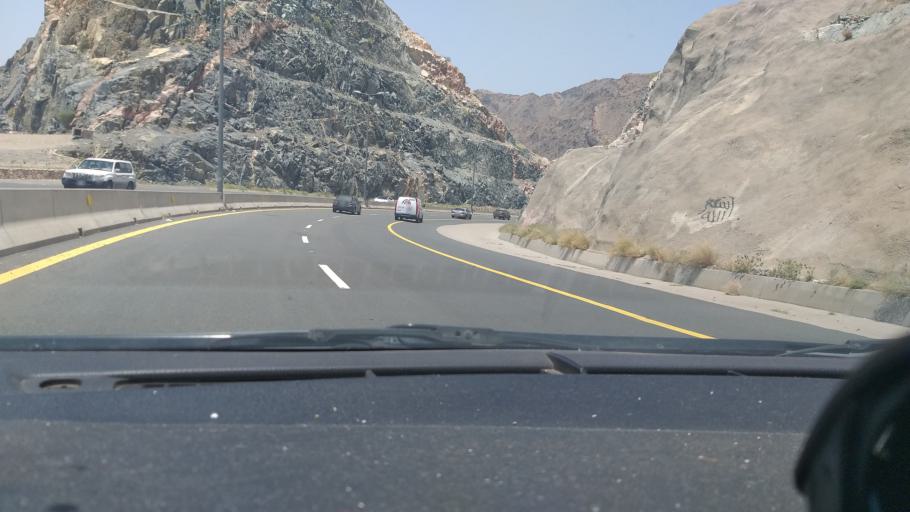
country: SA
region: Makkah
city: Al Hada
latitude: 21.3511
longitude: 40.2411
